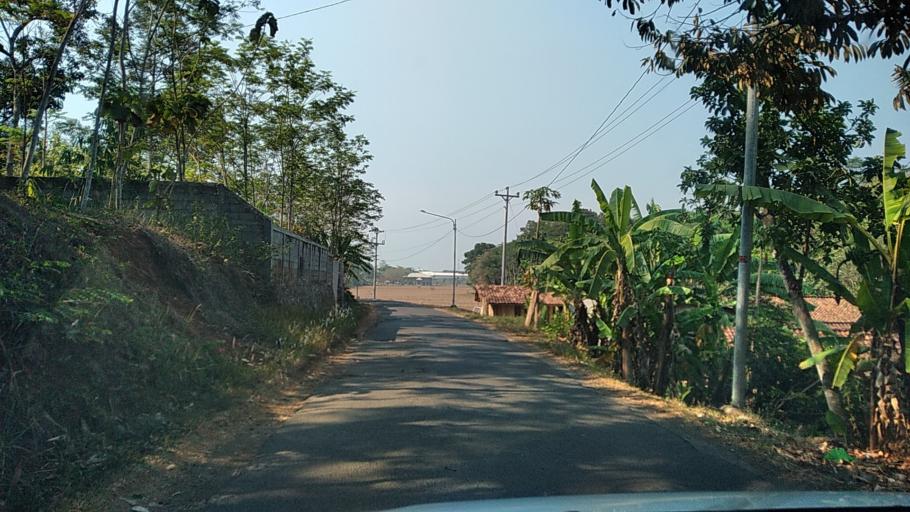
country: ID
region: Central Java
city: Ungaran
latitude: -7.0586
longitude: 110.3342
